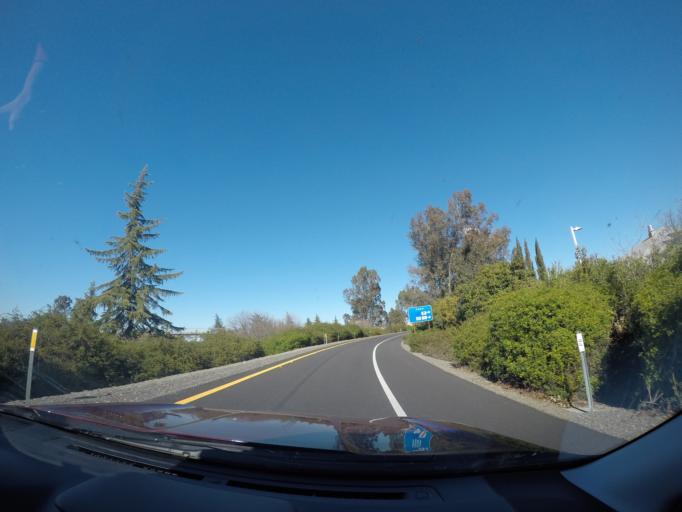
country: US
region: California
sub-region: Tehama County
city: Corning
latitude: 39.9267
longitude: -122.1997
